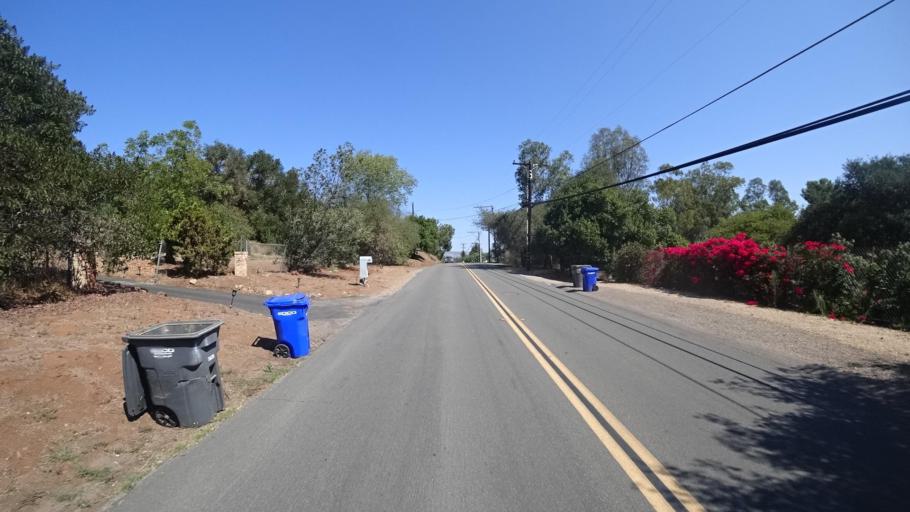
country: US
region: California
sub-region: San Diego County
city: Escondido
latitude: 33.0816
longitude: -117.0916
